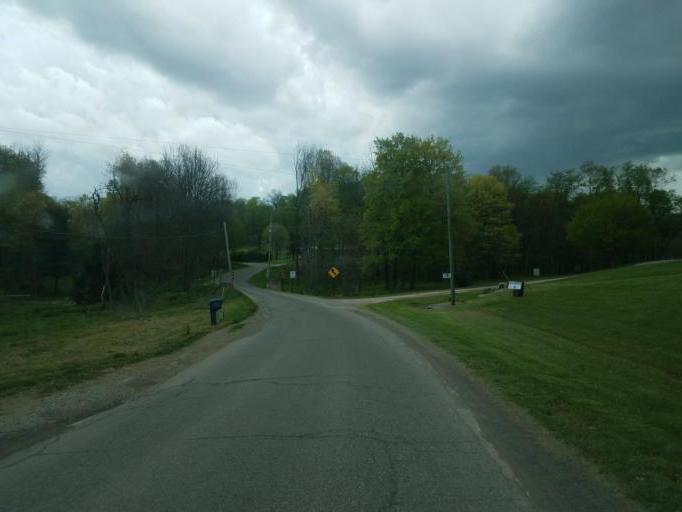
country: US
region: Ohio
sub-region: Knox County
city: Danville
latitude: 40.4508
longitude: -82.2229
